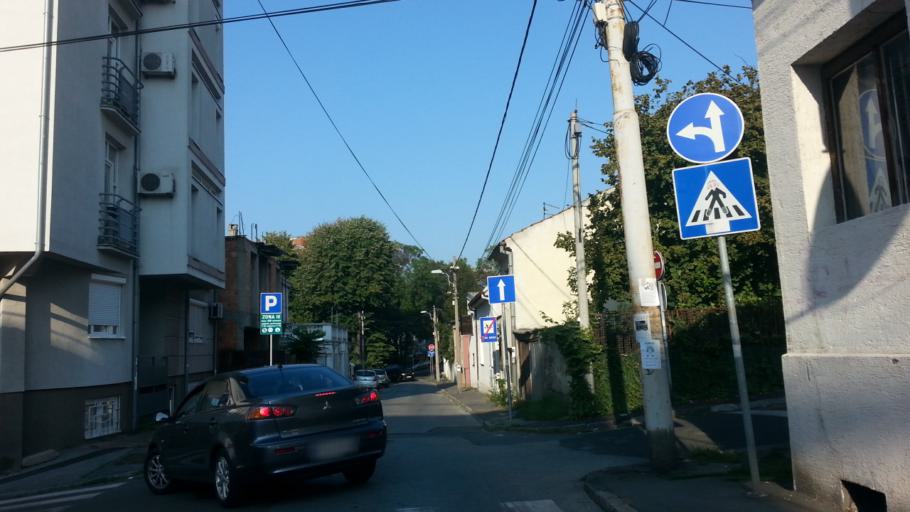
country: RS
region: Central Serbia
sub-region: Belgrade
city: Vracar
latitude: 44.7955
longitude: 20.4790
